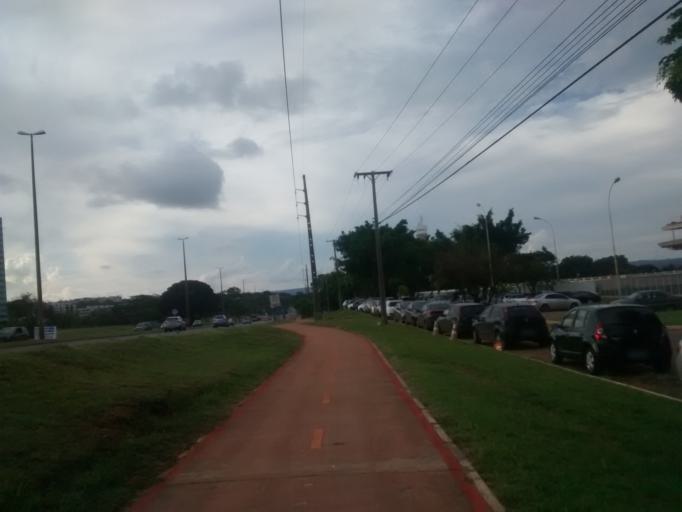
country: BR
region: Federal District
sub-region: Brasilia
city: Brasilia
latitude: -15.7891
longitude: -47.8732
